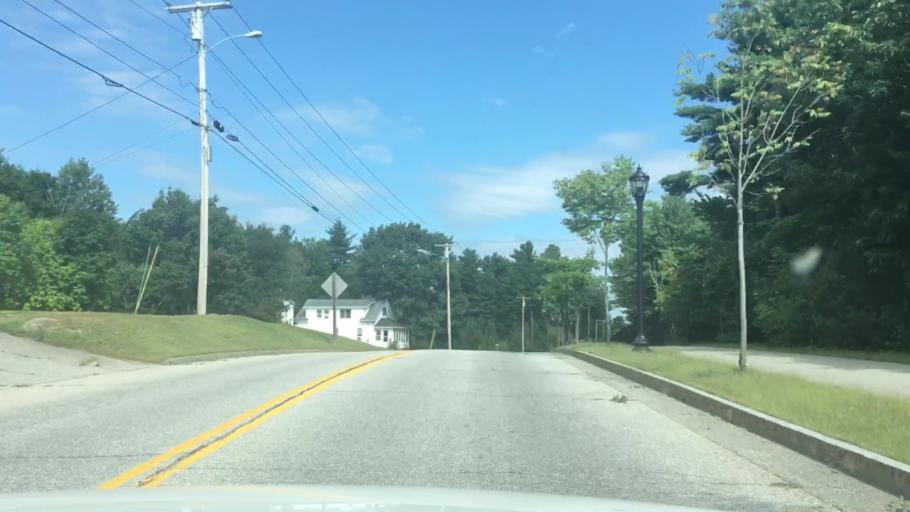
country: US
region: Maine
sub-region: Androscoggin County
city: Auburn
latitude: 44.0950
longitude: -70.2453
